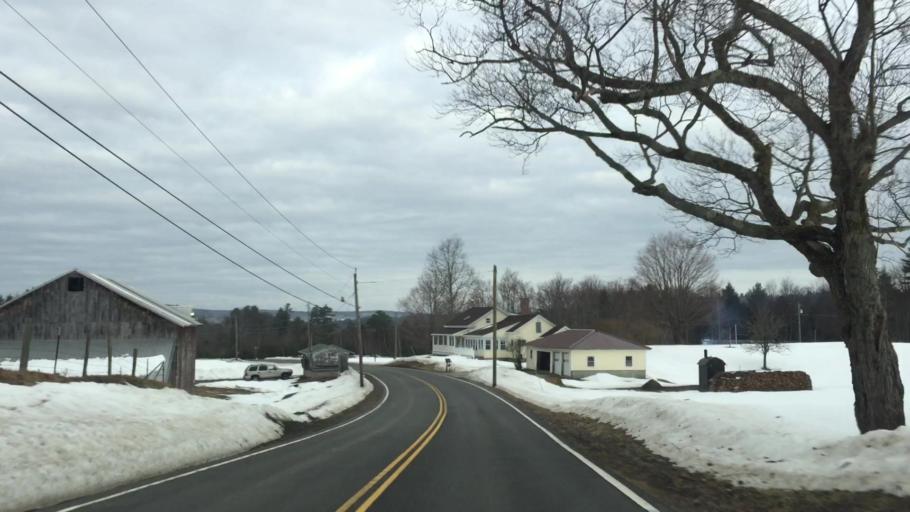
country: US
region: Massachusetts
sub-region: Berkshire County
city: Hinsdale
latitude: 42.4217
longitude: -73.0765
